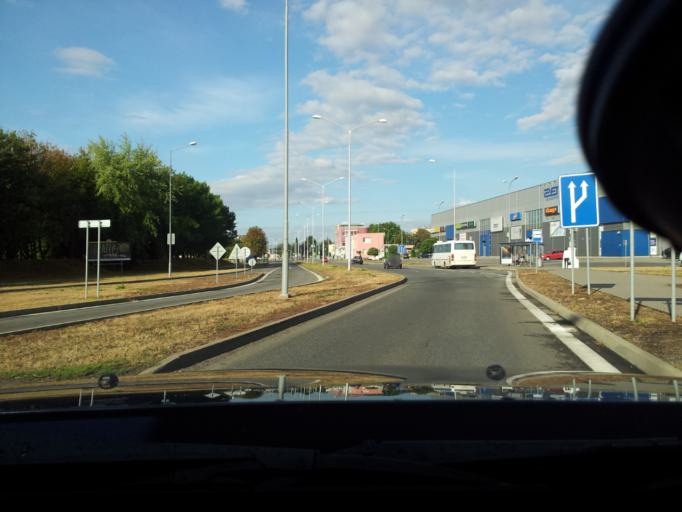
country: SK
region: Kosicky
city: Michalovce
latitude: 48.7593
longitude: 21.9182
